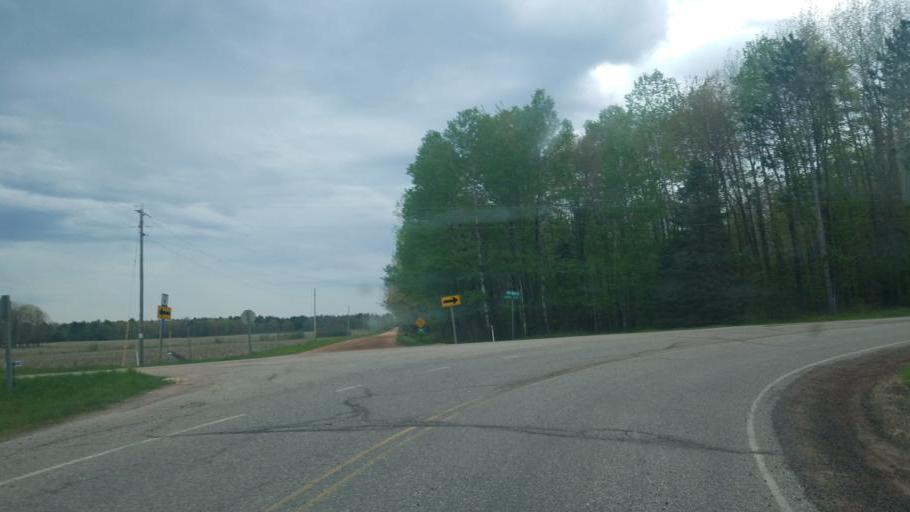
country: US
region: Wisconsin
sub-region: Wood County
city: Marshfield
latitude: 44.5126
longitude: -90.2990
